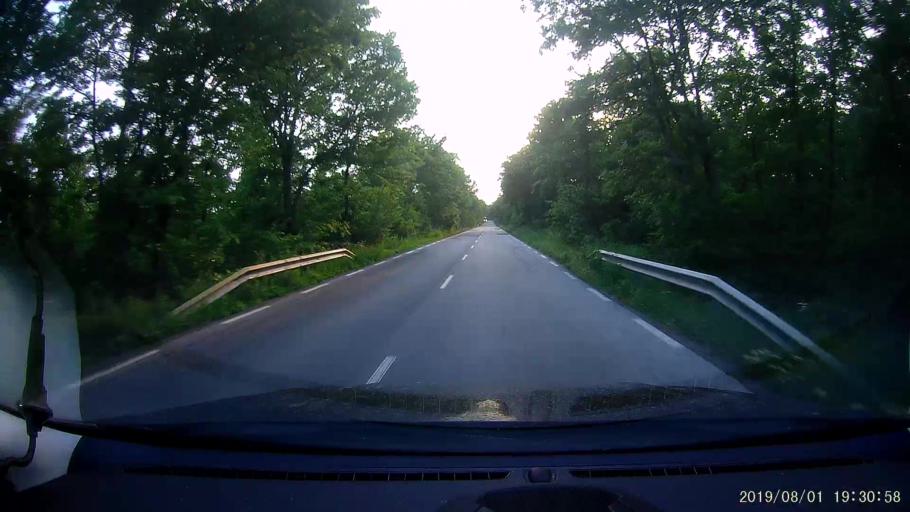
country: BG
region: Burgas
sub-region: Obshtina Sungurlare
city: Sungurlare
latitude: 42.8101
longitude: 26.8835
